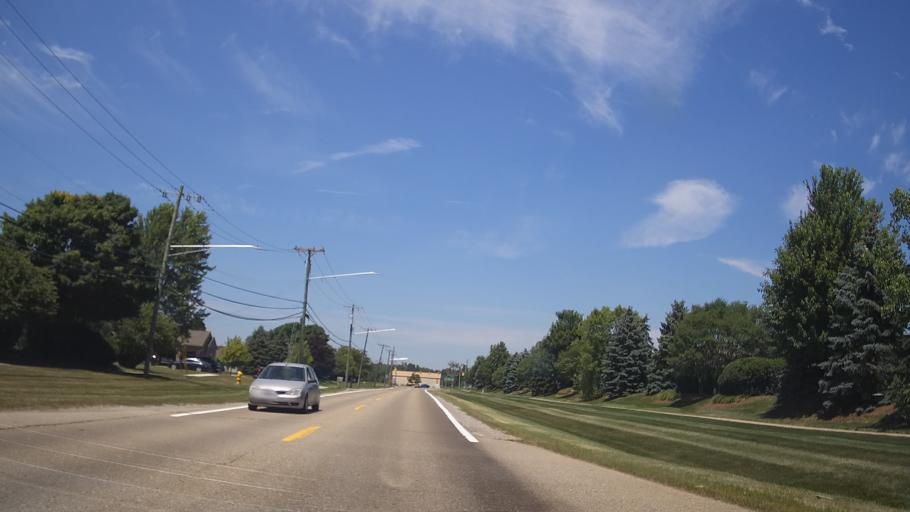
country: US
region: Michigan
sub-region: Macomb County
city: Clinton
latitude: 42.6550
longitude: -82.9171
